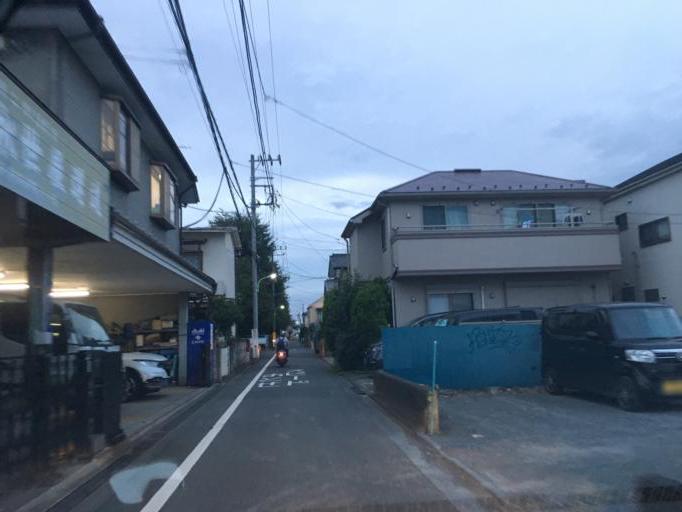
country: JP
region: Tokyo
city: Kokubunji
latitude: 35.7136
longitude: 139.4555
